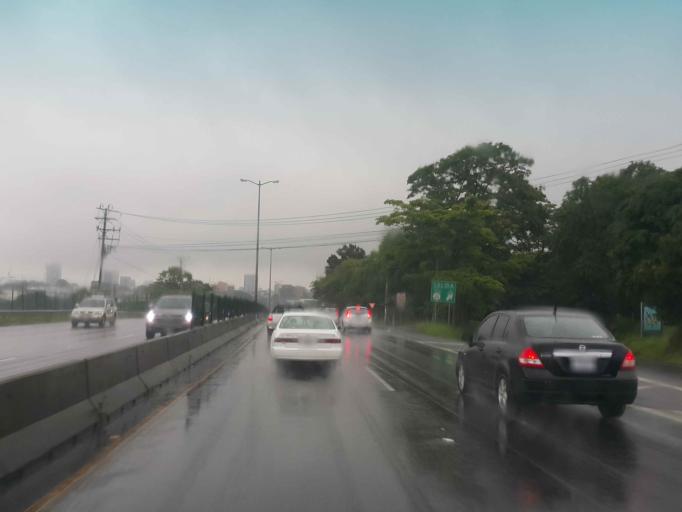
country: CR
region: San Jose
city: San Rafael
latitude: 9.9359
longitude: -84.1291
